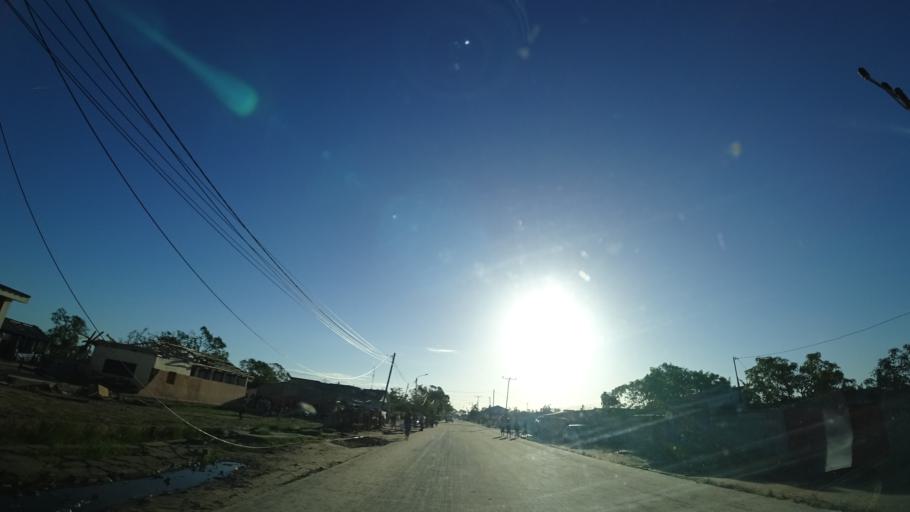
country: MZ
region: Sofala
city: Beira
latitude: -19.7434
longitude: 34.8422
